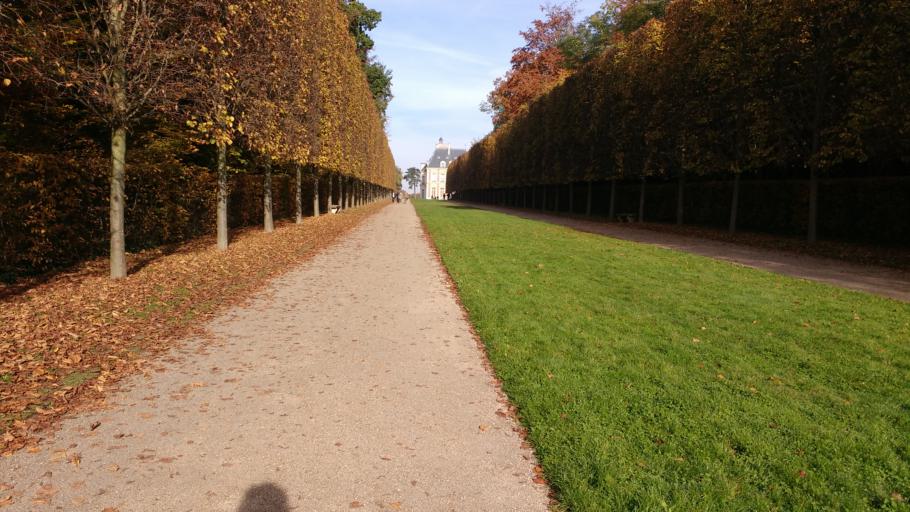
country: FR
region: Ile-de-France
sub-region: Departement des Hauts-de-Seine
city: Sceaux
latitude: 48.7718
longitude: 2.3008
